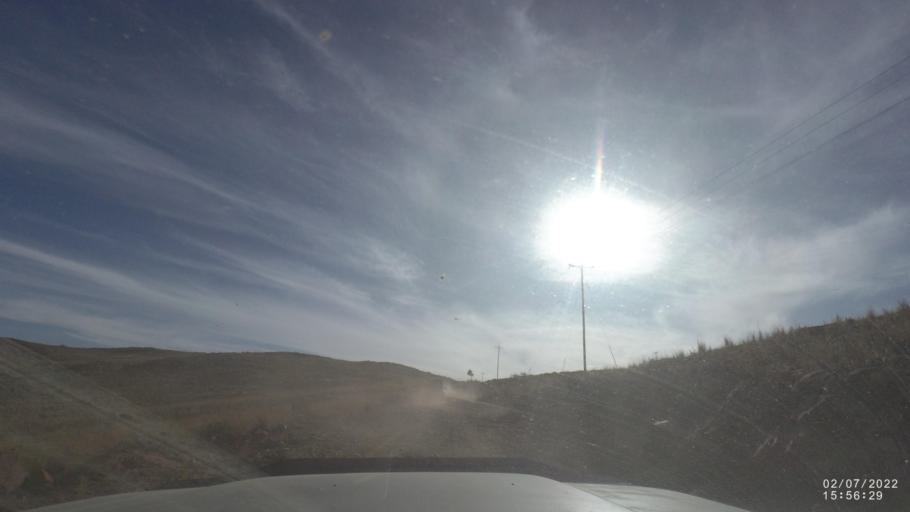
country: BO
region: Cochabamba
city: Irpa Irpa
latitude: -17.9091
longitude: -66.4251
